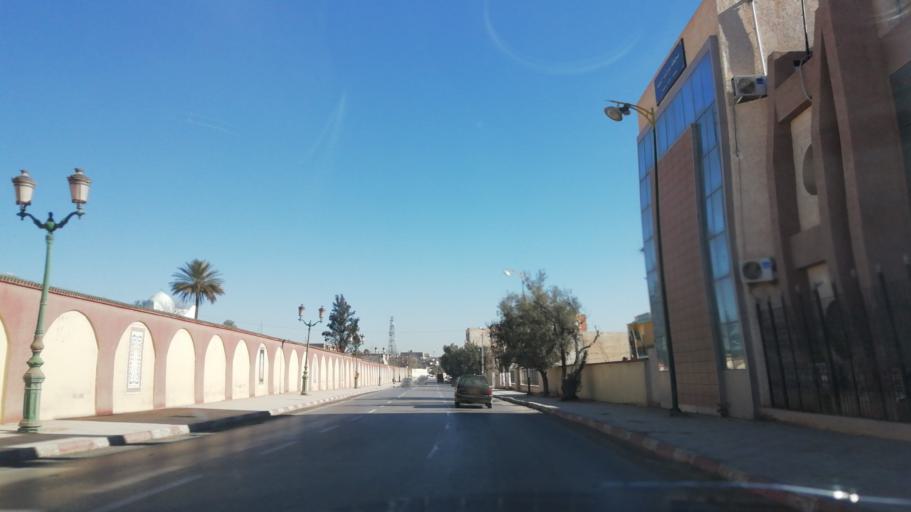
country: DZ
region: Tlemcen
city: Nedroma
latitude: 34.8464
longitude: -1.7363
